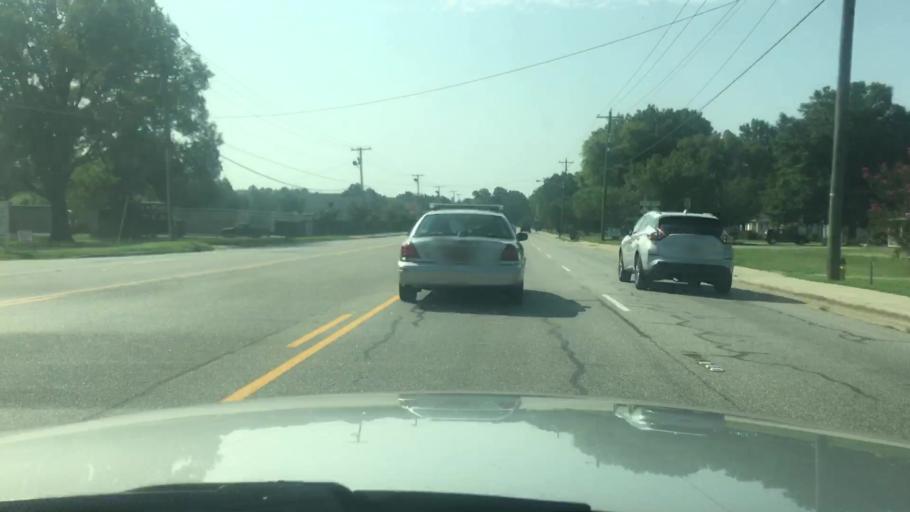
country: US
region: North Carolina
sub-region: Cumberland County
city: Vander
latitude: 35.0171
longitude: -78.8385
